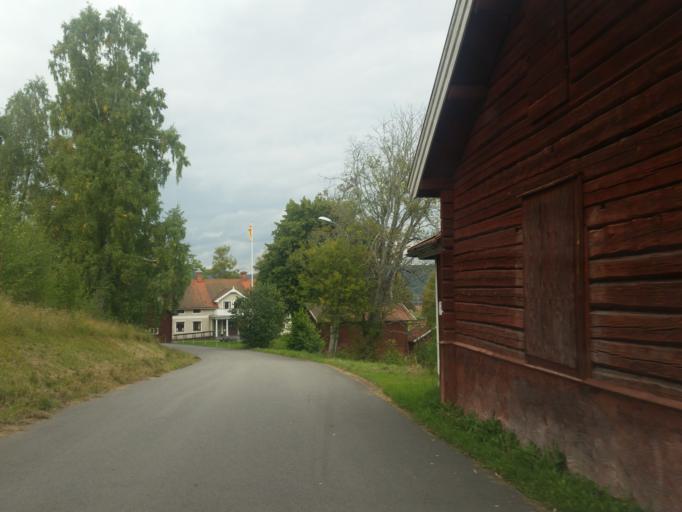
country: SE
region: Dalarna
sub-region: Leksand Municipality
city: Smedby
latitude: 60.6809
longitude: 15.1019
